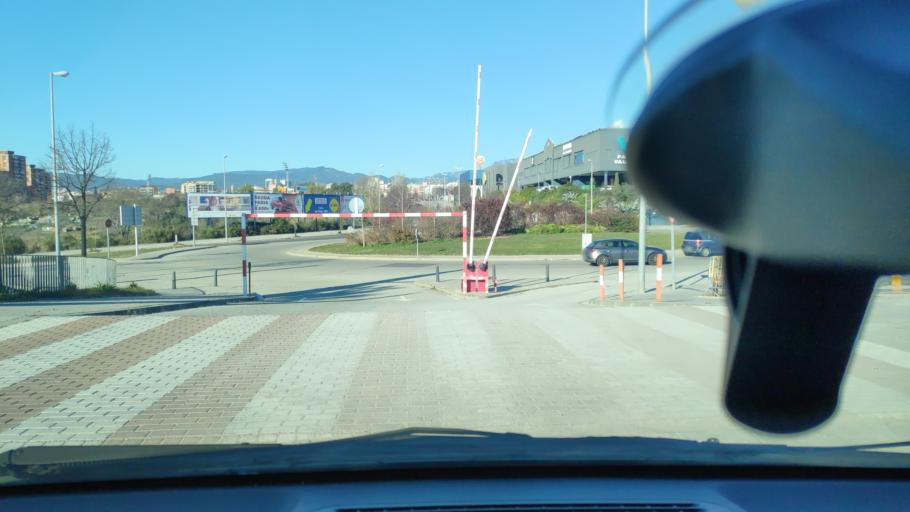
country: ES
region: Catalonia
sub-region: Provincia de Barcelona
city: Terrassa
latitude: 41.5444
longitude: 2.0244
